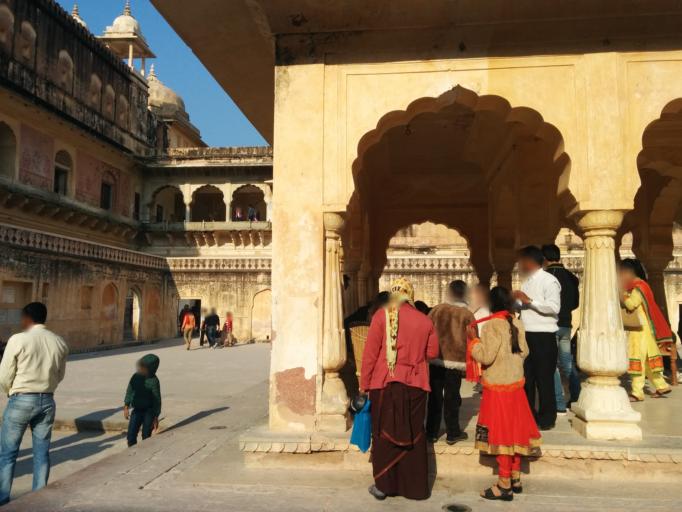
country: IN
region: Rajasthan
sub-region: Jaipur
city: Jaipur
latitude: 26.9854
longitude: 75.8500
